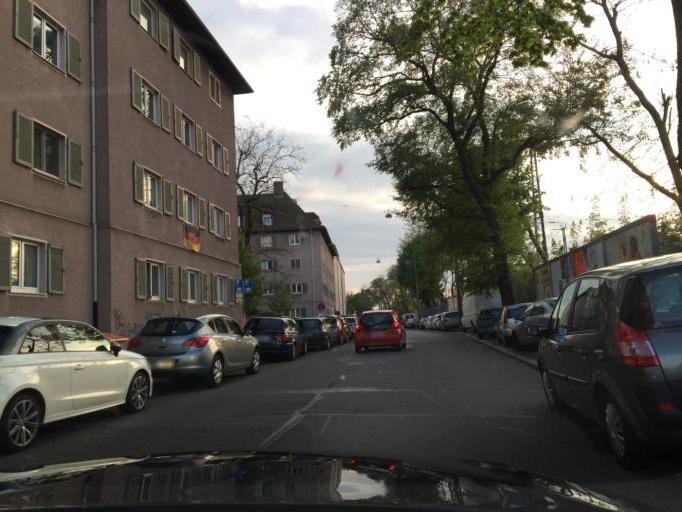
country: DE
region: Bavaria
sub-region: Regierungsbezirk Mittelfranken
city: Nuernberg
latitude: 49.4418
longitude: 11.0676
